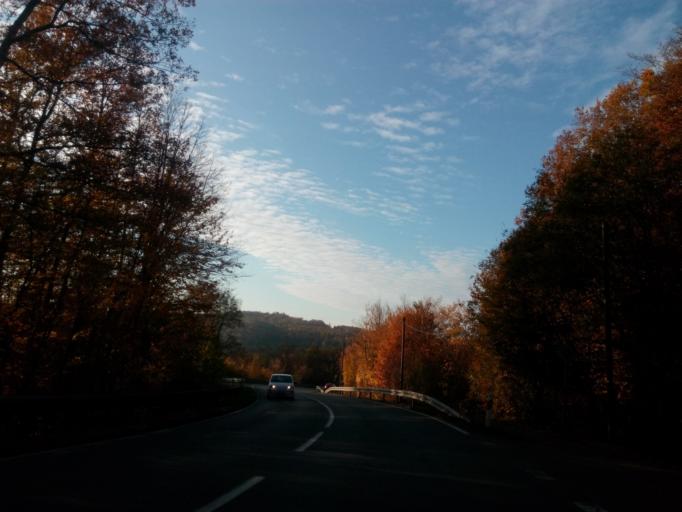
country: DE
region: Saarland
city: Sulzbach
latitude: 49.2853
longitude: 7.0103
